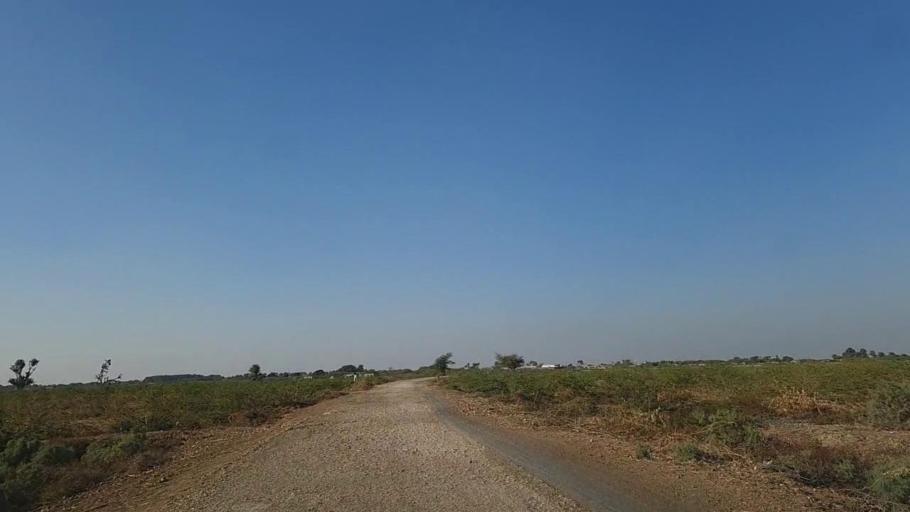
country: PK
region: Sindh
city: Samaro
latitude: 25.3576
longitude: 69.3763
